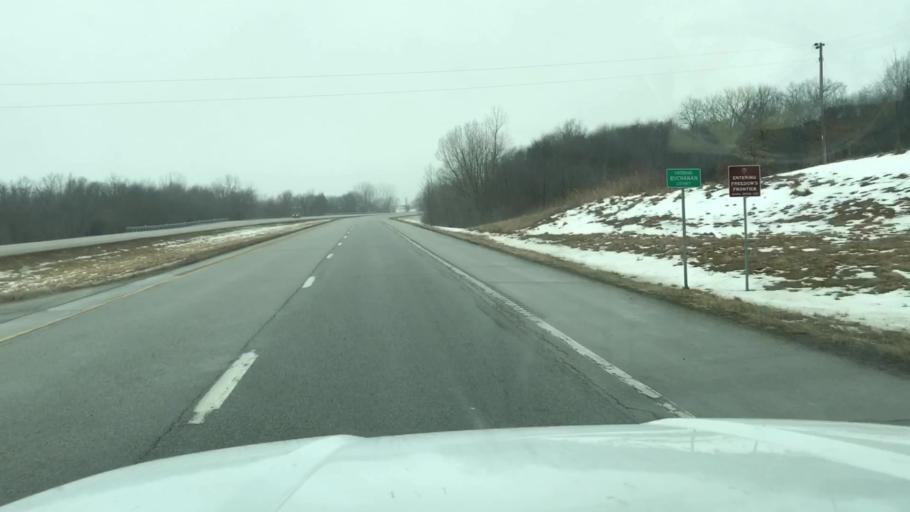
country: US
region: Missouri
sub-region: Clinton County
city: Gower
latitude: 39.7486
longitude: -94.6025
